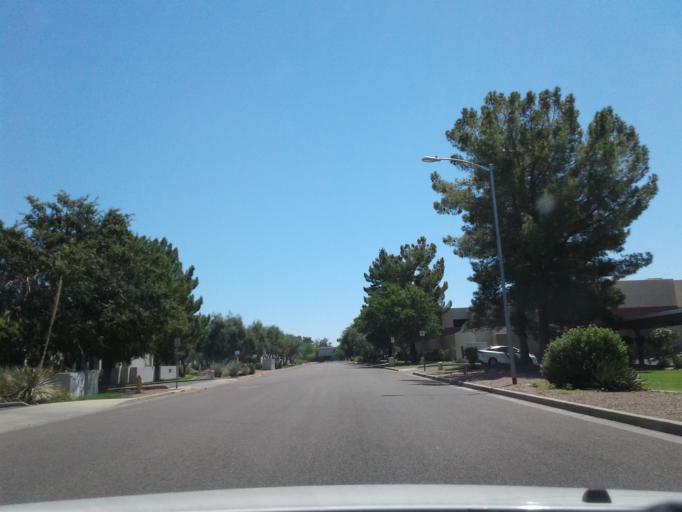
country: US
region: Arizona
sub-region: Maricopa County
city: Guadalupe
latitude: 33.3975
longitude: -112.0187
